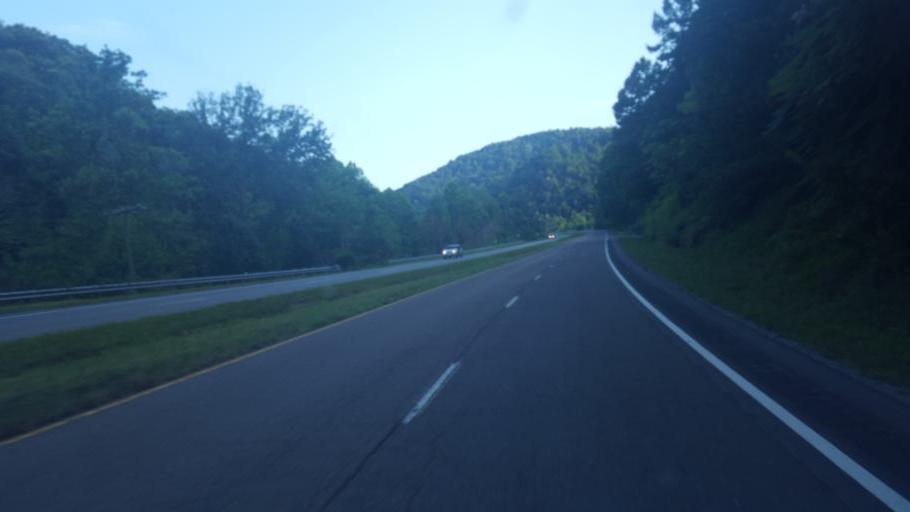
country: US
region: Tennessee
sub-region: Hawkins County
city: Church Hill
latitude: 36.6785
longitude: -82.7555
